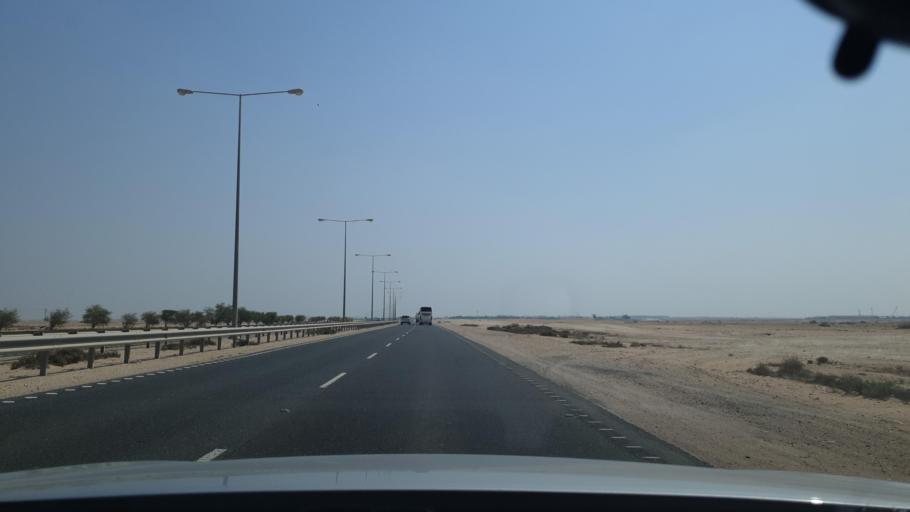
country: QA
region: Al Khawr
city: Al Khawr
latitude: 25.7464
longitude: 51.4810
